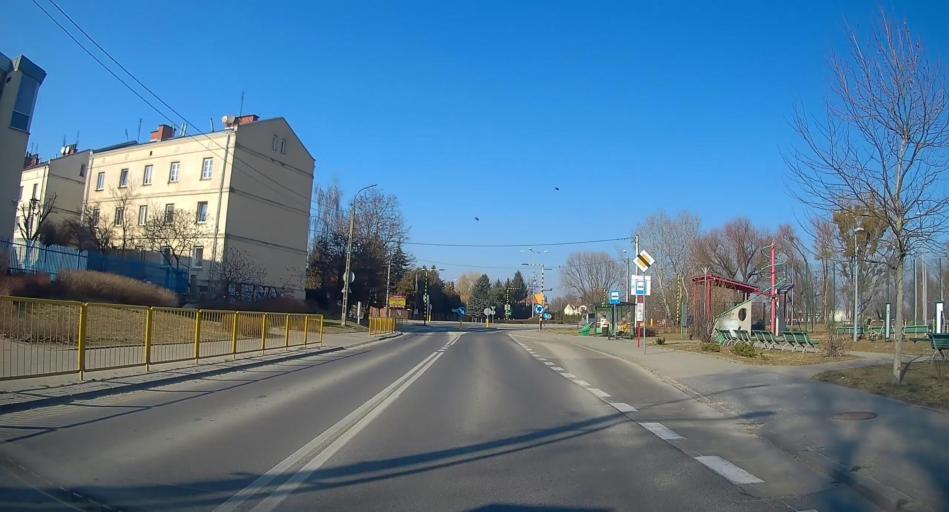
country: PL
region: Masovian Voivodeship
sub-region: Powiat piaseczynski
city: Konstancin-Jeziorna
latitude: 52.1008
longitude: 21.1254
